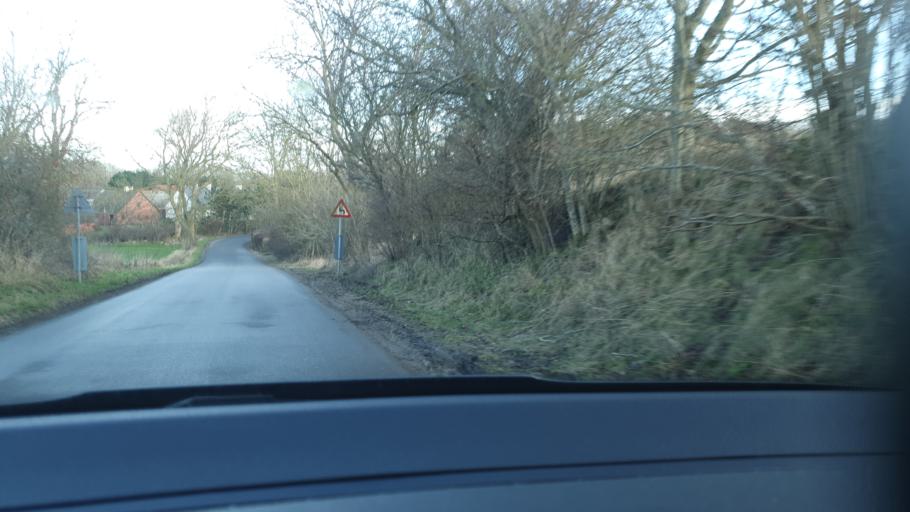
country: DK
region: Zealand
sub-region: Odsherred Kommune
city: Nykobing Sjaelland
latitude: 55.9217
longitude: 11.6355
